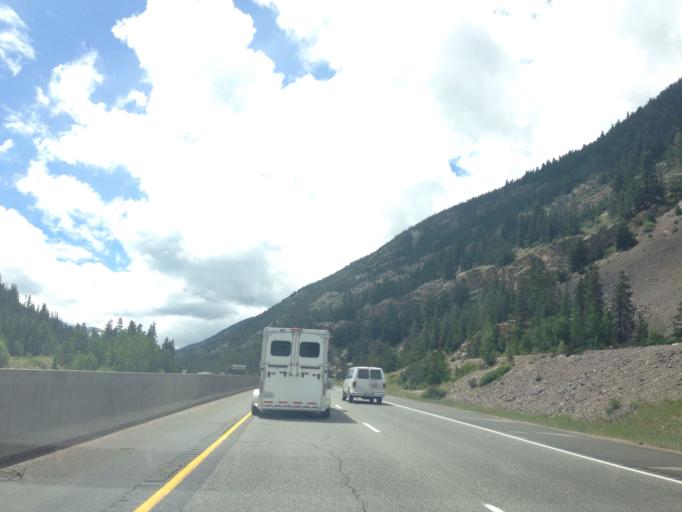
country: US
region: Colorado
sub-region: Clear Creek County
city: Georgetown
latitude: 39.6963
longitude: -105.7431
